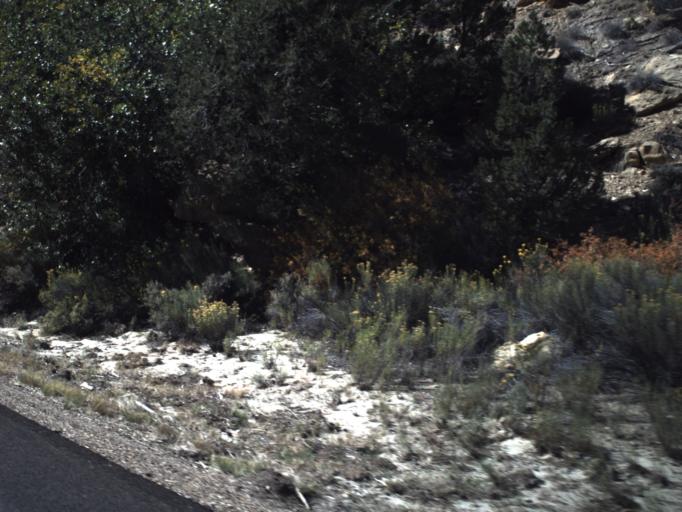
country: US
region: Utah
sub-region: Garfield County
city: Panguitch
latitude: 37.6093
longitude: -111.9016
